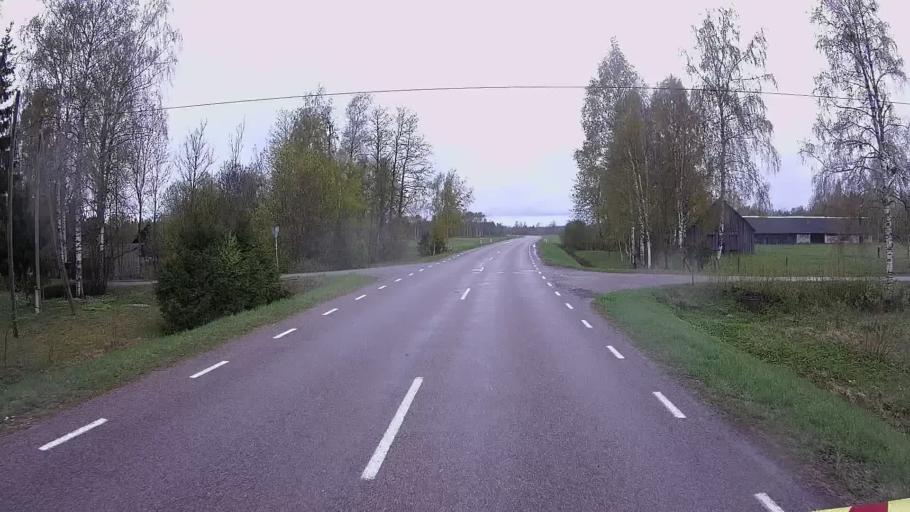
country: EE
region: Hiiumaa
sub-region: Kaerdla linn
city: Kardla
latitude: 58.7142
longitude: 22.5771
